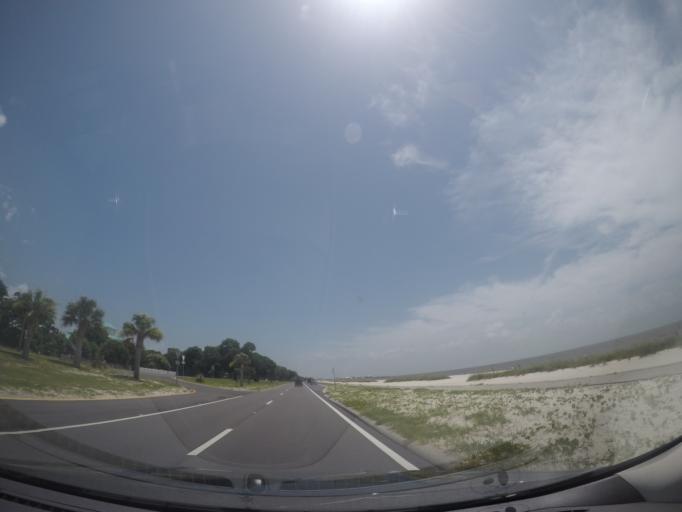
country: US
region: Mississippi
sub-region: Harrison County
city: Pass Christian
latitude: 30.3094
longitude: -89.2625
